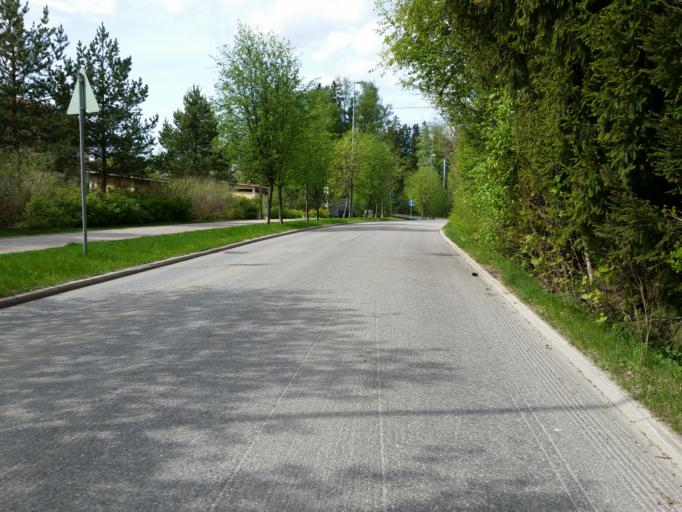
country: FI
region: Uusimaa
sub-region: Helsinki
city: Espoo
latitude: 60.2127
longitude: 24.6400
